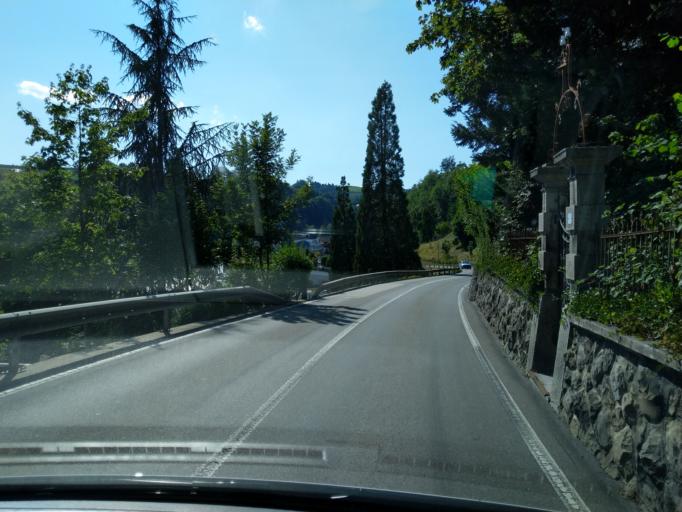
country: CH
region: Lucerne
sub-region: Entlebuch District
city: Wolhusen
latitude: 47.0557
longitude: 8.0866
